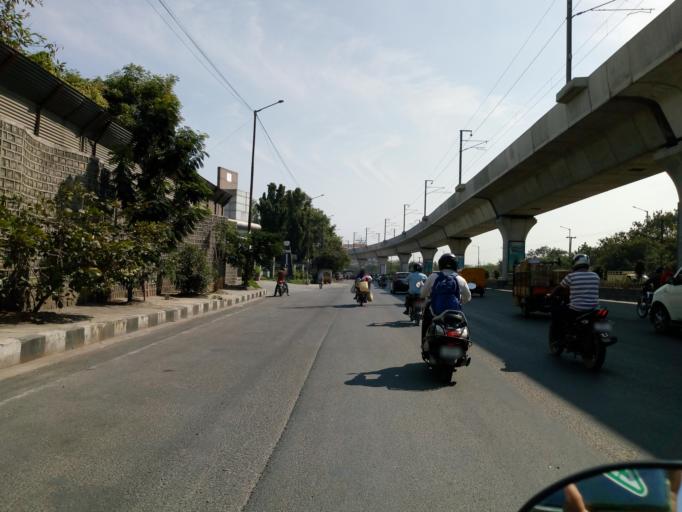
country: IN
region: Telangana
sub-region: Hyderabad
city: Malkajgiri
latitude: 17.4236
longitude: 78.5372
